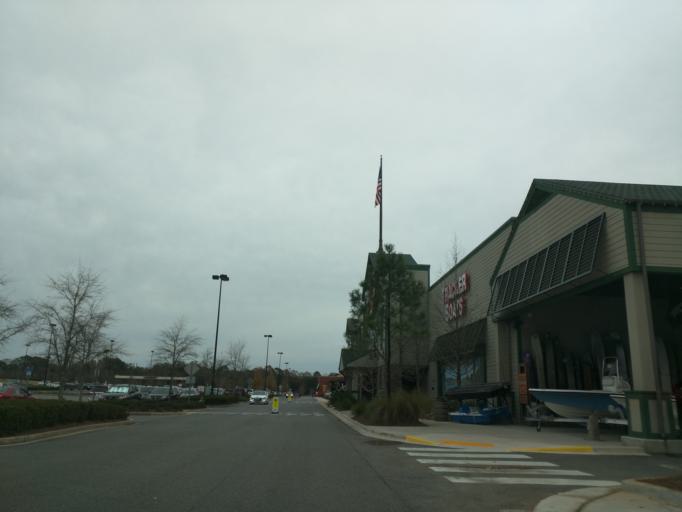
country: US
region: Florida
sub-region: Leon County
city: Tallahassee
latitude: 30.4611
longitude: -84.2146
